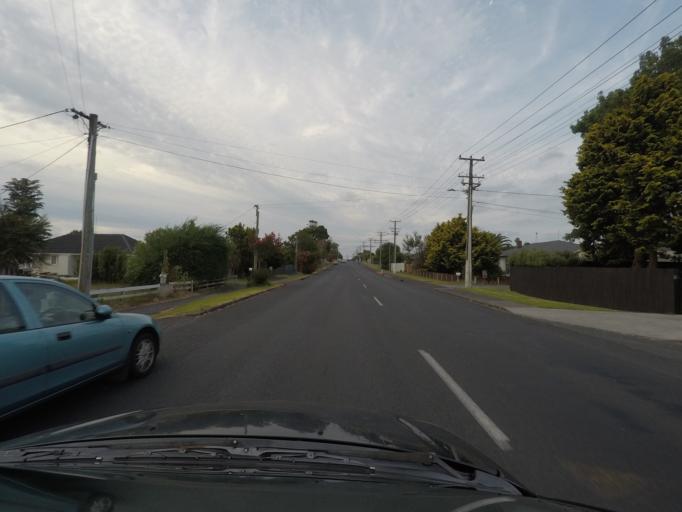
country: NZ
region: Auckland
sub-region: Auckland
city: Rosebank
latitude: -36.8372
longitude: 174.6506
